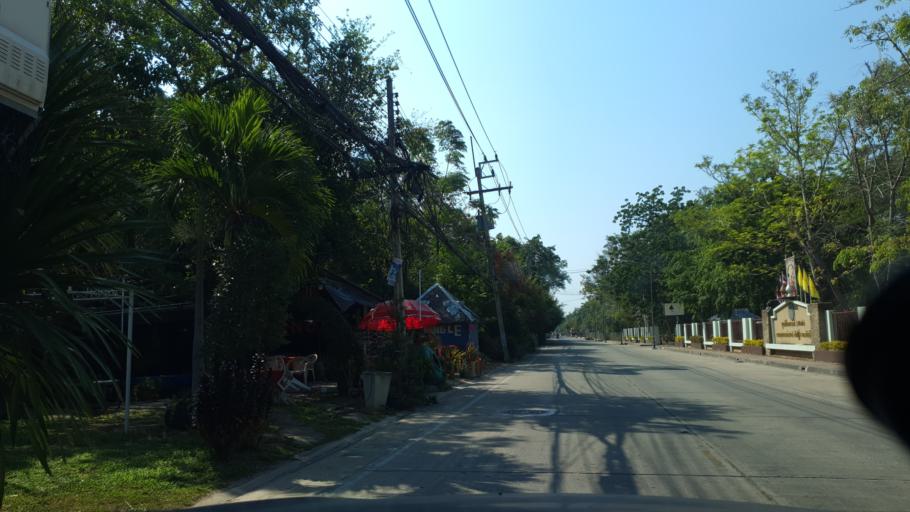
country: TH
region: Phetchaburi
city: Cha-am
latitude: 12.8001
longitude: 99.9839
